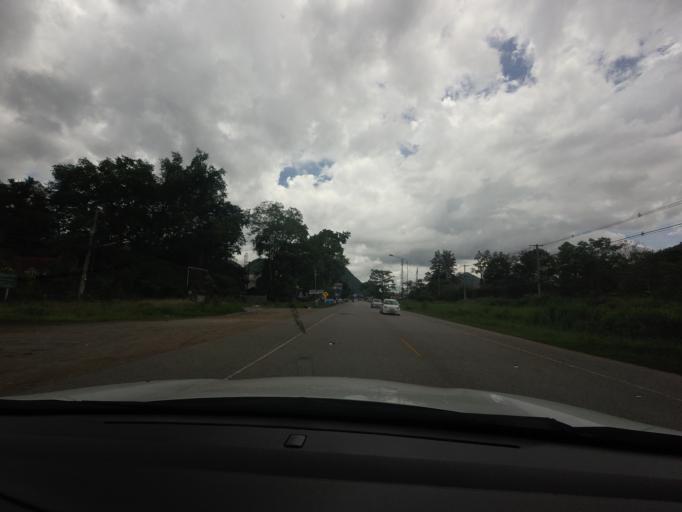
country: TH
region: Nakhon Ratchasima
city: Pak Chong
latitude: 14.5347
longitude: 101.3741
